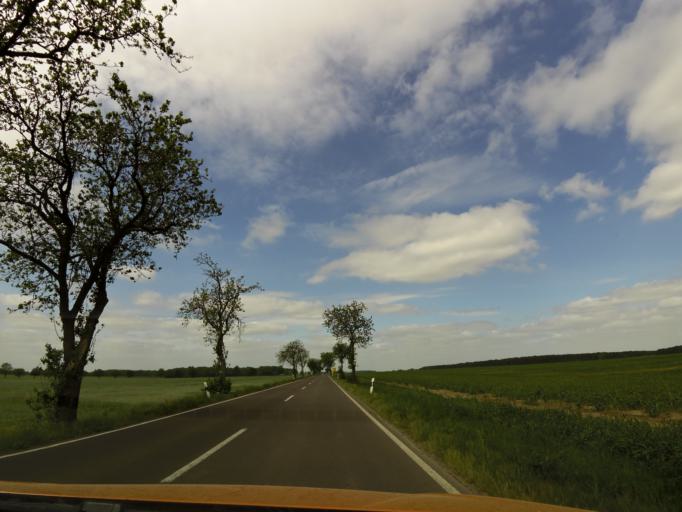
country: DE
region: Saxony-Anhalt
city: Loburg
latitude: 52.1090
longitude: 12.1564
